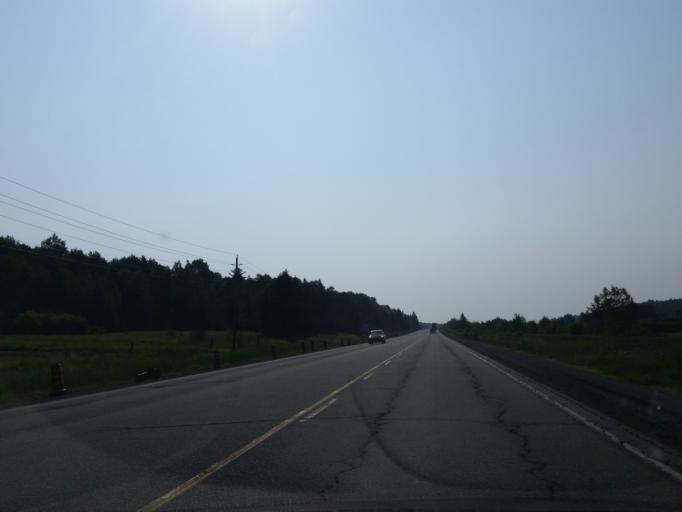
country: CA
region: Ontario
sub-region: Nipissing District
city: North Bay
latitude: 46.4279
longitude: -80.2070
